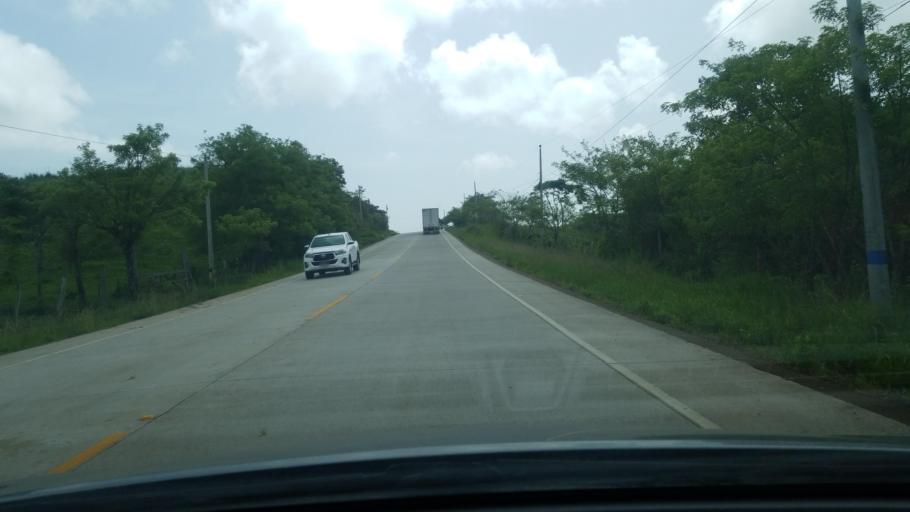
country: HN
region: Copan
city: San Jeronimo
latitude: 14.9371
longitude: -88.9197
